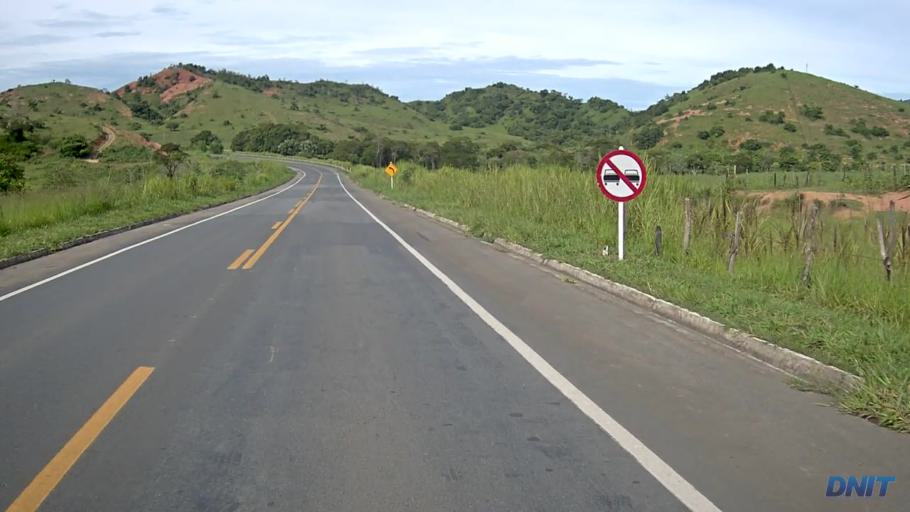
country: BR
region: Minas Gerais
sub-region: Belo Oriente
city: Belo Oriente
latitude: -19.2190
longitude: -42.3091
